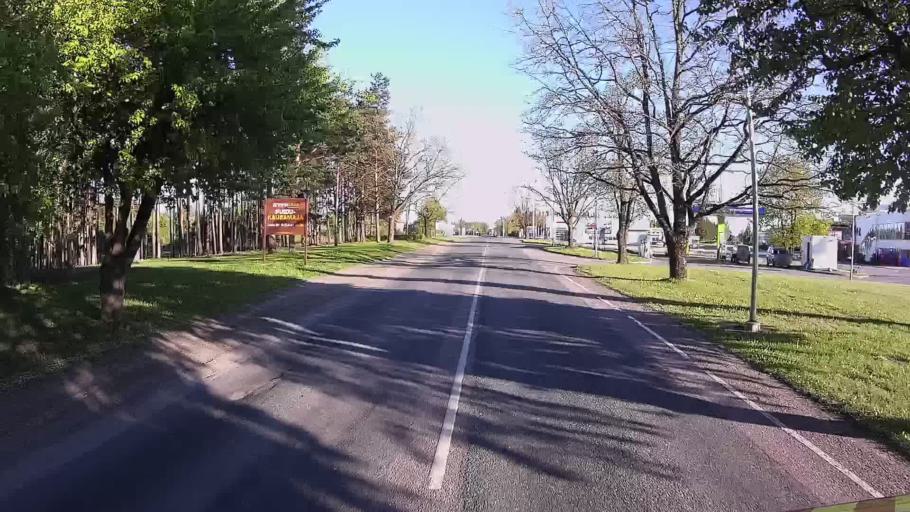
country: EE
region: Viljandimaa
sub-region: Viljandi linn
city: Viljandi
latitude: 58.3792
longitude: 25.5954
